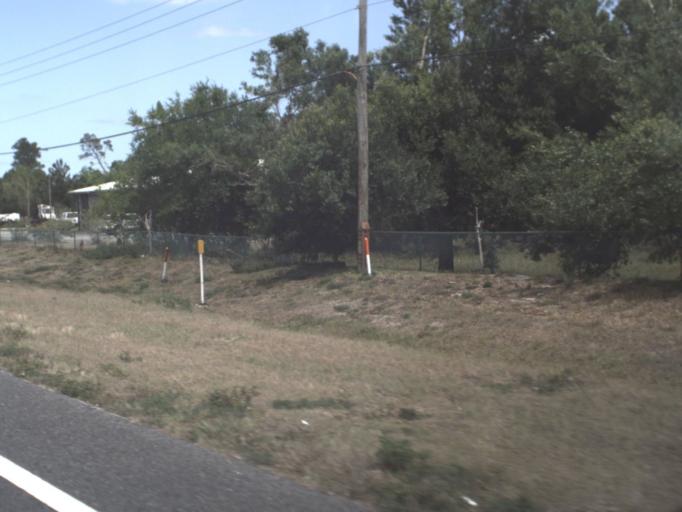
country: US
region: Florida
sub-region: Brevard County
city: Titusville
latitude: 28.5433
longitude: -80.8312
